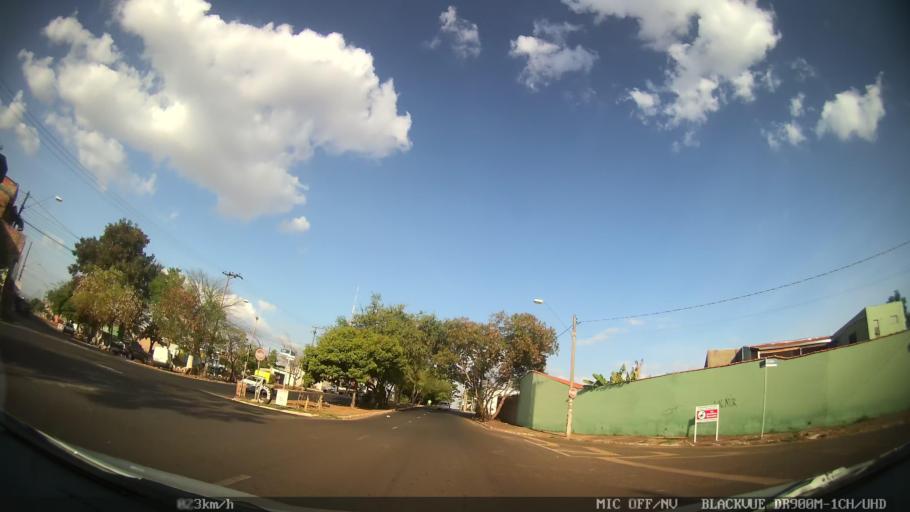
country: BR
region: Sao Paulo
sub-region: Ribeirao Preto
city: Ribeirao Preto
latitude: -21.1554
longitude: -47.8410
